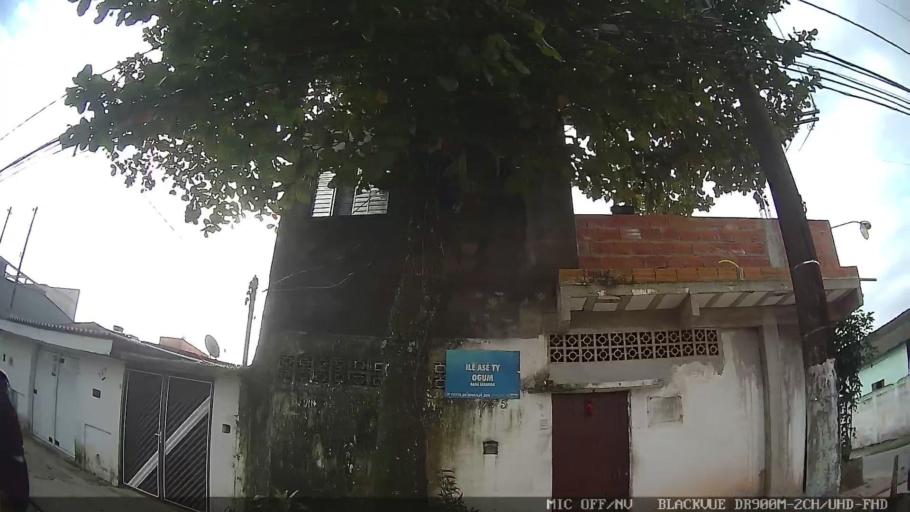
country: BR
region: Sao Paulo
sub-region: Santos
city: Santos
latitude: -23.9502
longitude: -46.2869
